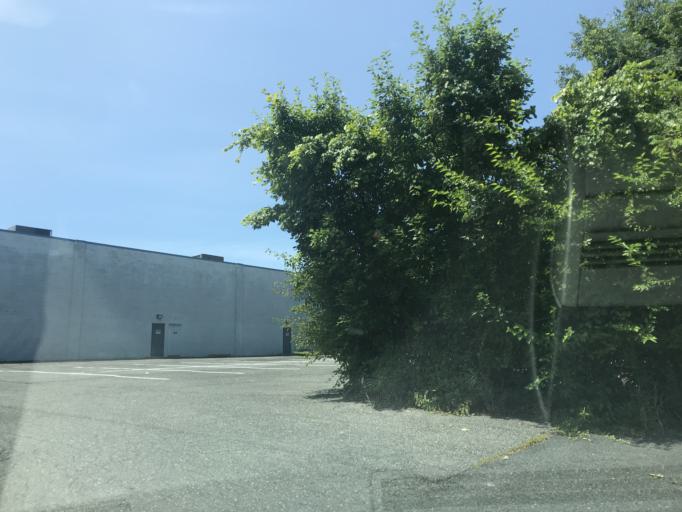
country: US
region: Maryland
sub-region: Harford County
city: South Bel Air
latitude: 39.5571
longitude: -76.2758
